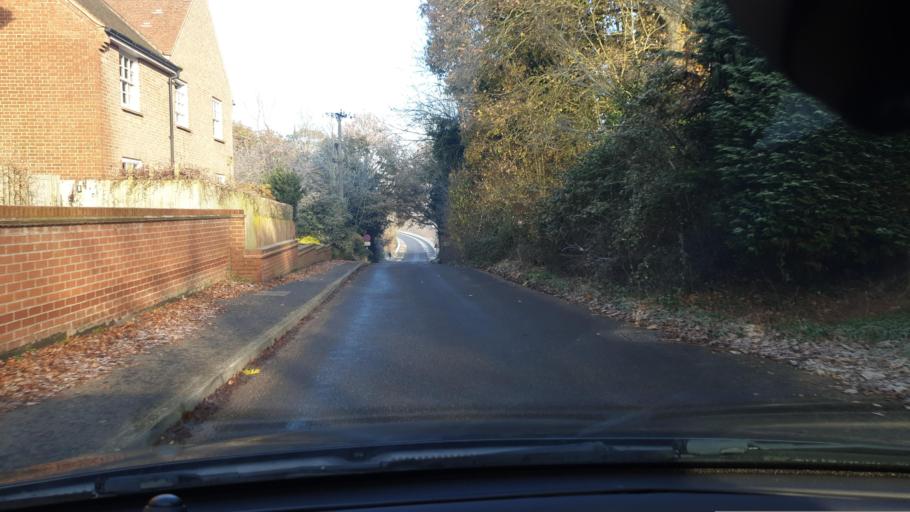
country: GB
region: England
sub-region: Essex
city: Mistley
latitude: 51.9927
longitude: 1.1103
